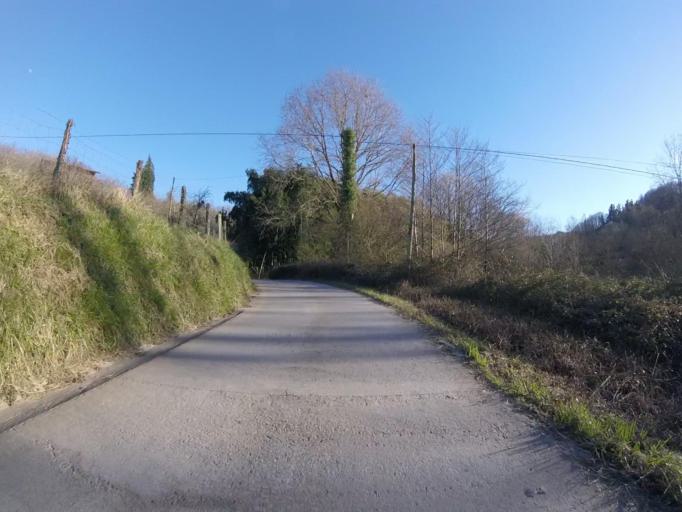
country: ES
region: Basque Country
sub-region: Provincia de Guipuzcoa
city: Errenteria
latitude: 43.2868
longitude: -1.8711
